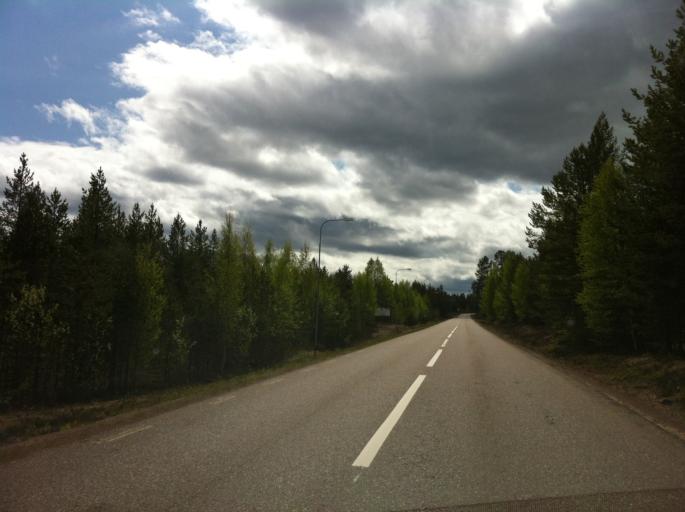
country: NO
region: Hedmark
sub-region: Trysil
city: Innbygda
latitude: 61.6852
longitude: 13.1284
